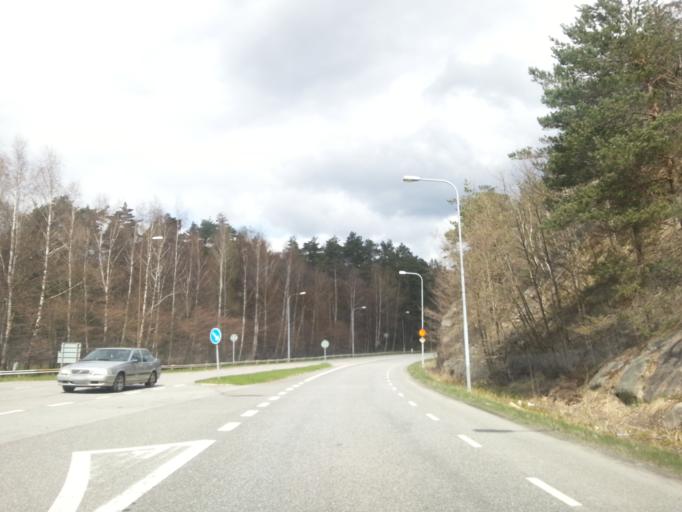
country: SE
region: Vaestra Goetaland
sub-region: Goteborg
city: Hammarkullen
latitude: 57.7768
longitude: 12.0210
